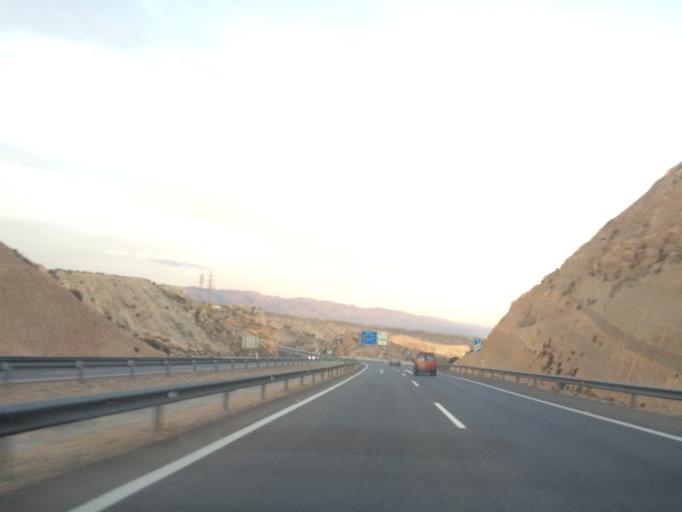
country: ES
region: Andalusia
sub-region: Provincia de Almeria
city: Almeria
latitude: 36.8488
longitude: -2.4788
